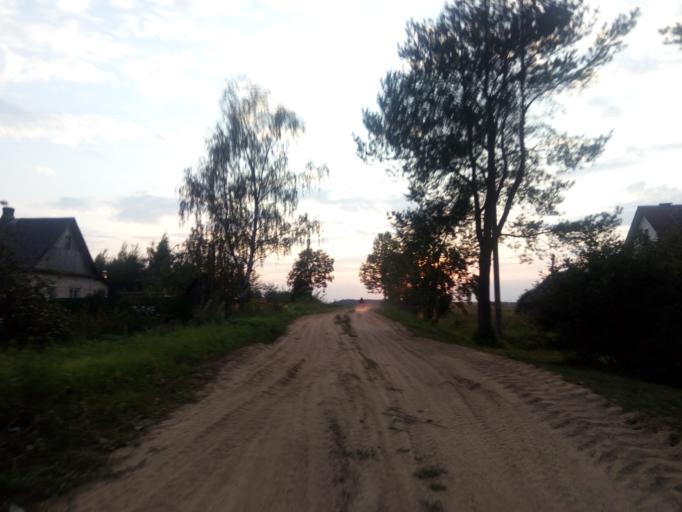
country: BY
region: Vitebsk
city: Dzisna
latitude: 55.6613
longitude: 28.3245
